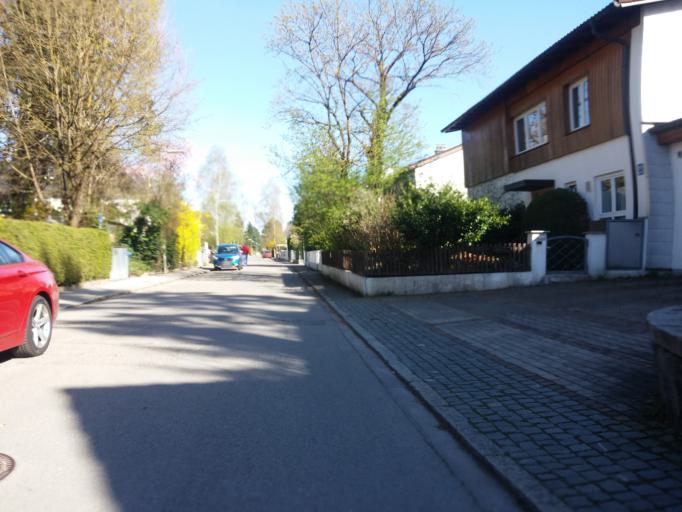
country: DE
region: Bavaria
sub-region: Upper Bavaria
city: Neubiberg
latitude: 48.0804
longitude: 11.6655
